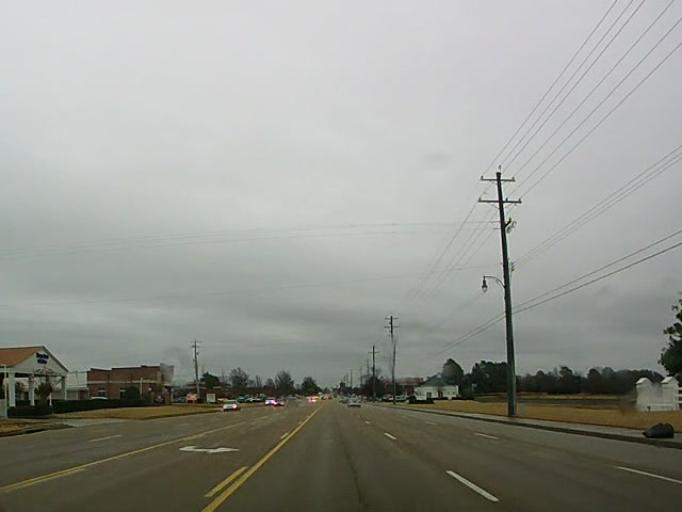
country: US
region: Tennessee
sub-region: Shelby County
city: Collierville
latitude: 35.0465
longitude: -89.7035
